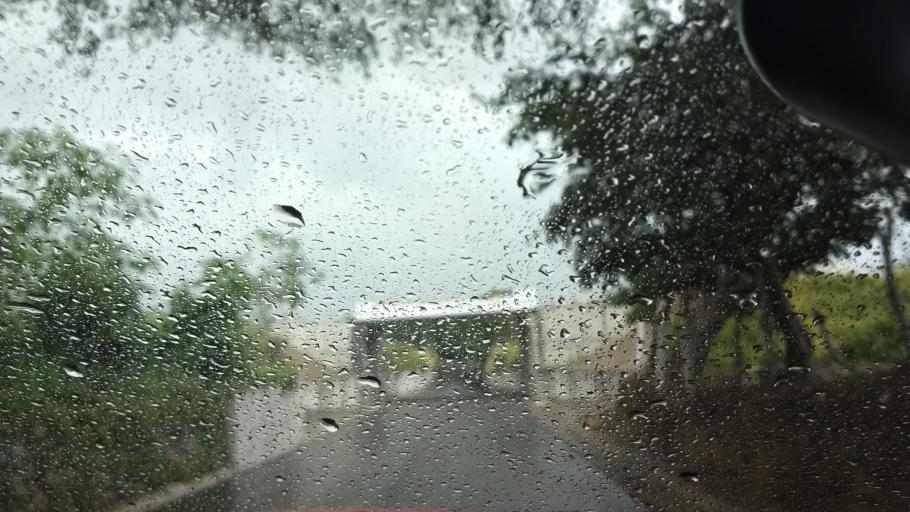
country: MX
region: Jalisco
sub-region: Tonila
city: San Marcos
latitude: 19.4409
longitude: -103.4917
